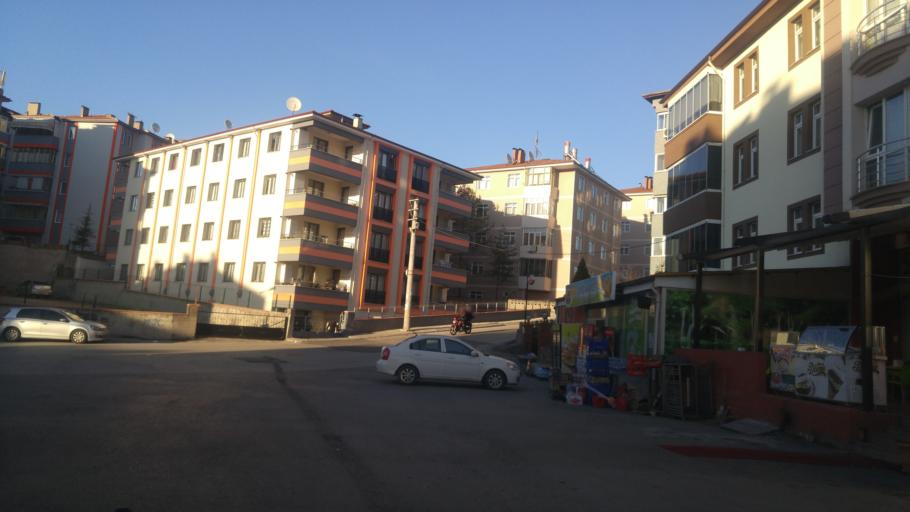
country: TR
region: Karabuk
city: Safranbolu
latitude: 41.2256
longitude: 32.6663
